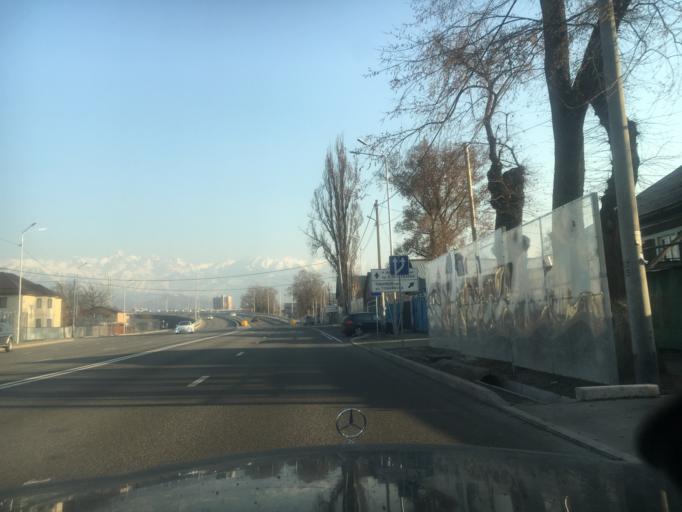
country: KZ
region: Almaty Qalasy
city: Almaty
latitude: 43.2800
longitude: 76.9400
